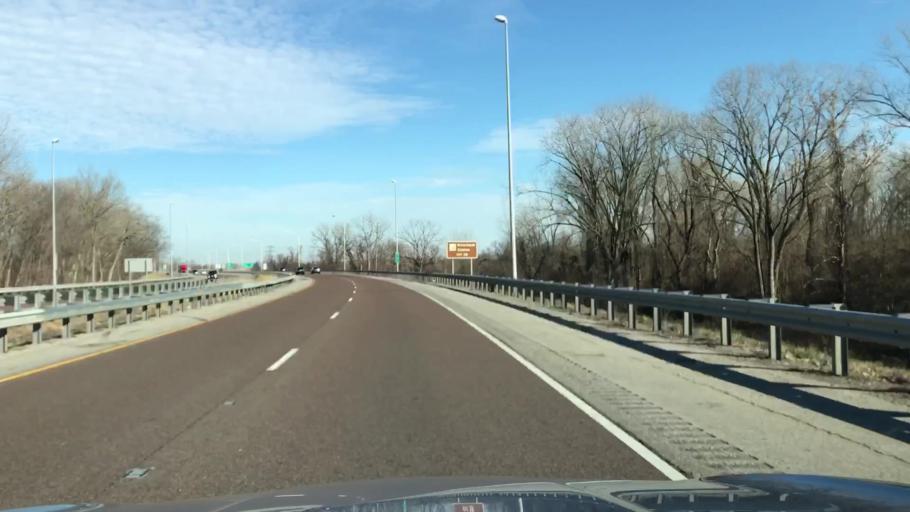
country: US
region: Missouri
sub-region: Saint Louis County
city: Glasgow Village
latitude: 38.7613
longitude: -90.1538
